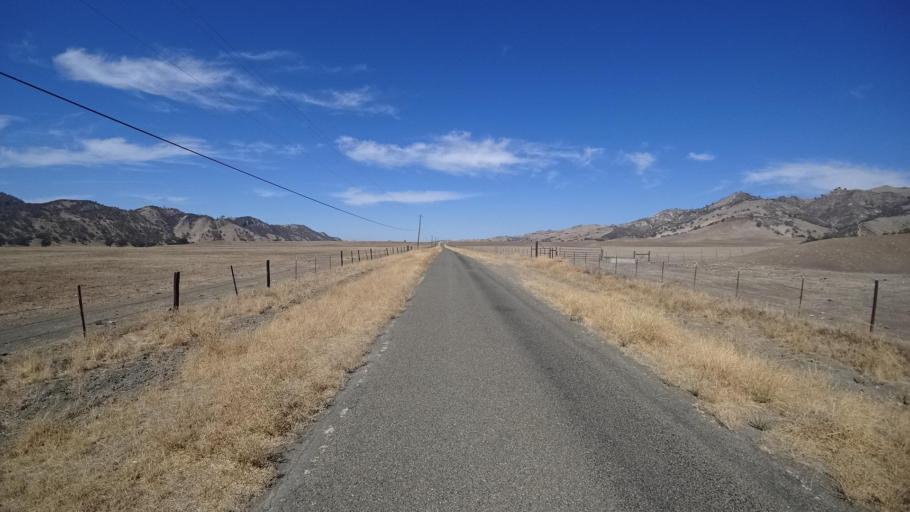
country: US
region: California
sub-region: Monterey County
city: King City
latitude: 36.1585
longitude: -120.7697
